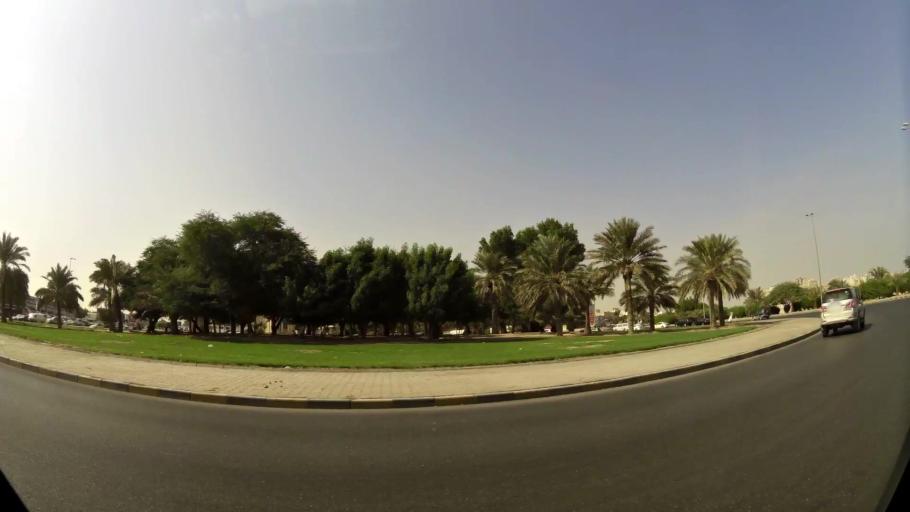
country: KW
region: Al Ahmadi
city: Al Fahahil
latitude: 29.0737
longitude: 48.1260
